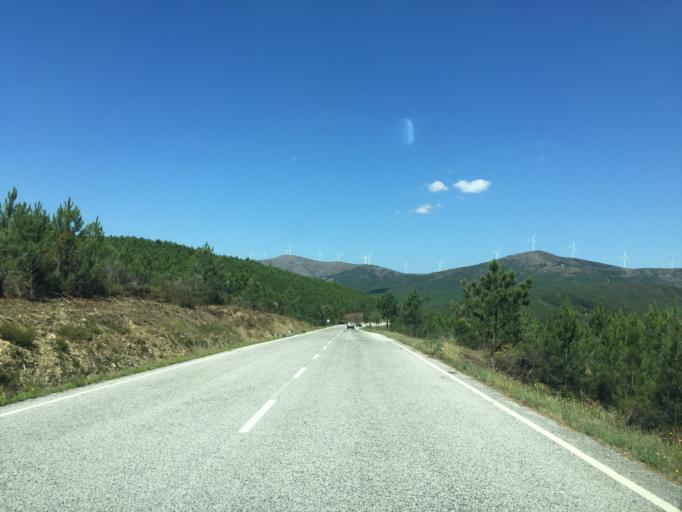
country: PT
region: Coimbra
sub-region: Pampilhosa da Serra
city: Pampilhosa da Serra
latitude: 40.1251
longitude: -7.8051
